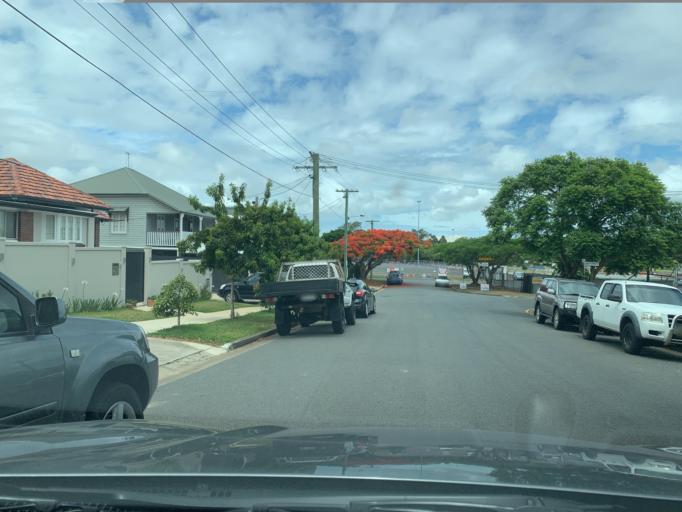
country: AU
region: Queensland
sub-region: Brisbane
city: Ascot
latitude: -27.4332
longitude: 153.0773
